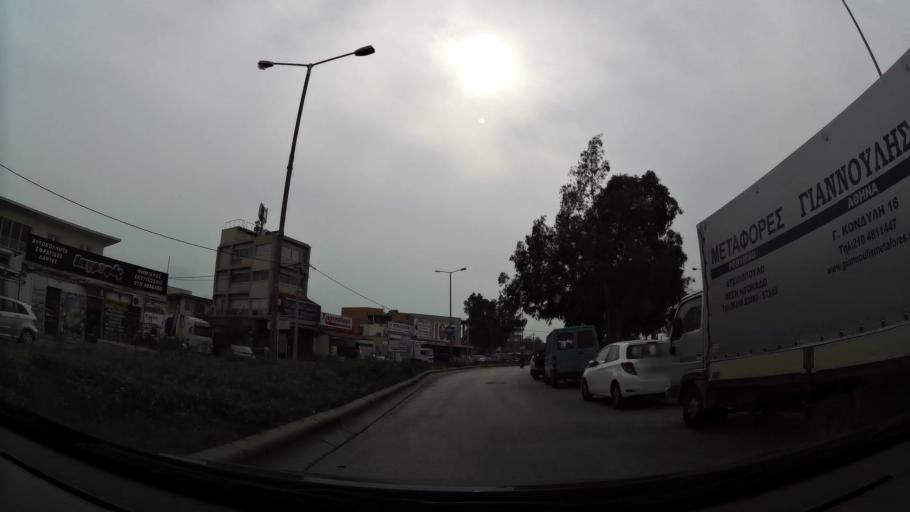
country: GR
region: Attica
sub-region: Nomarchia Athinas
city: Moskhaton
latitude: 37.9604
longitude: 23.6822
